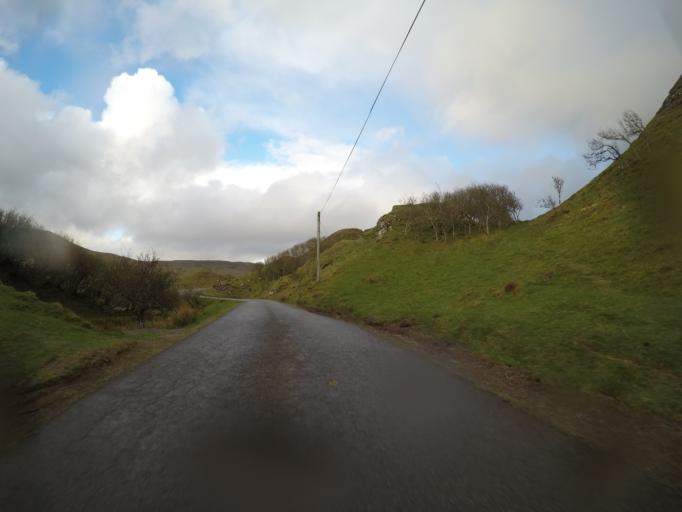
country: GB
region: Scotland
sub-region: Highland
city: Portree
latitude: 57.5836
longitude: -6.3302
